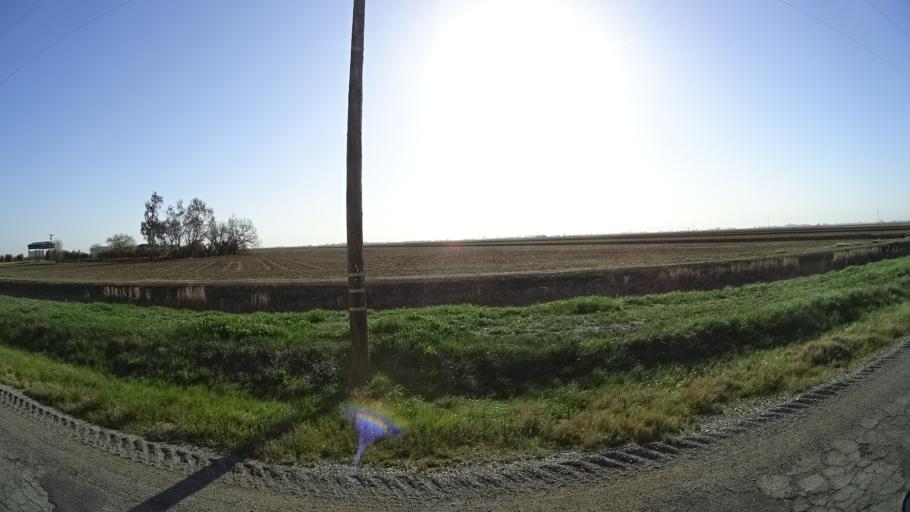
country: US
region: California
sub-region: Colusa County
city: Maxwell
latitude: 39.3873
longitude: -122.2298
